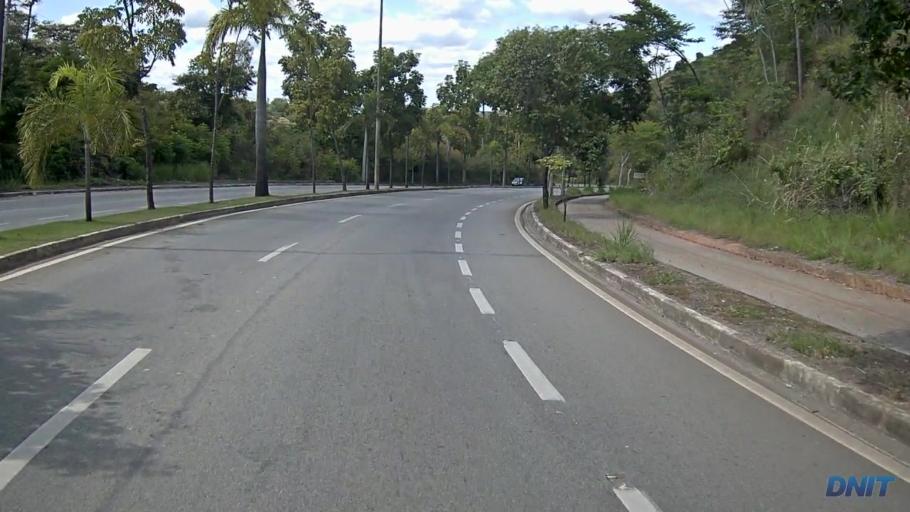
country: BR
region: Minas Gerais
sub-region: Coronel Fabriciano
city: Coronel Fabriciano
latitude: -19.5071
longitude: -42.5865
